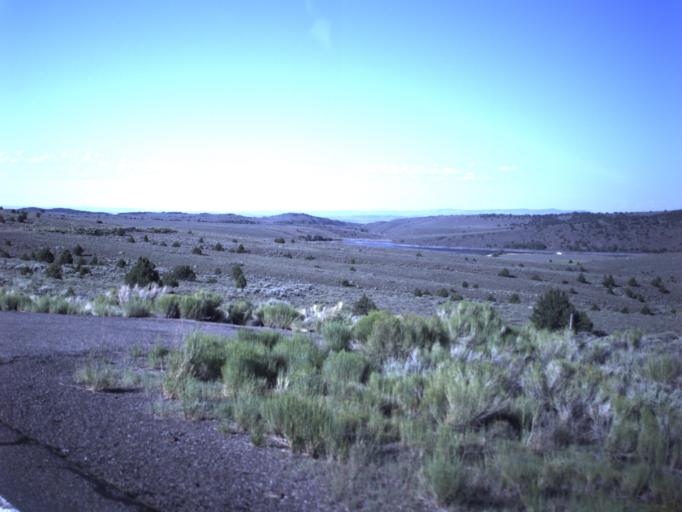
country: US
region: Utah
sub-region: Wayne County
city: Loa
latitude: 38.5317
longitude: -111.5145
